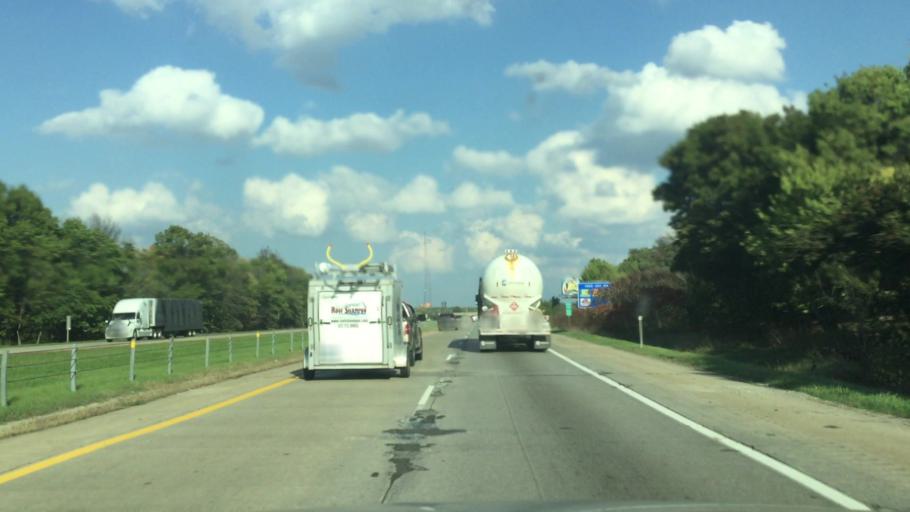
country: US
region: Michigan
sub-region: Calhoun County
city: Brownlee Park
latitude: 42.2956
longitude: -85.0982
